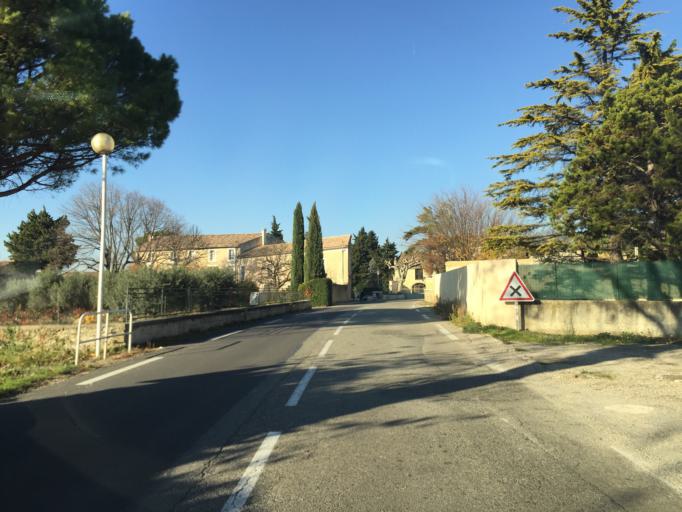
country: FR
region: Provence-Alpes-Cote d'Azur
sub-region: Departement du Vaucluse
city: Sainte-Cecile-les-Vignes
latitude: 44.2446
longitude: 4.8928
